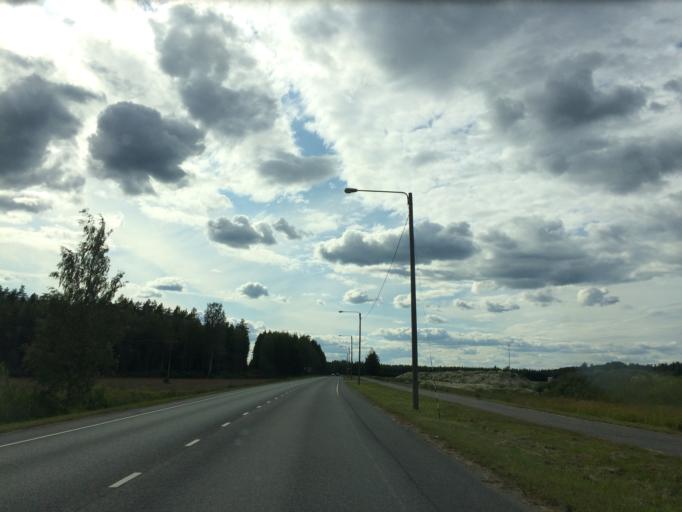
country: FI
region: Haeme
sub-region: Haemeenlinna
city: Janakkala
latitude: 60.9210
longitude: 24.6092
